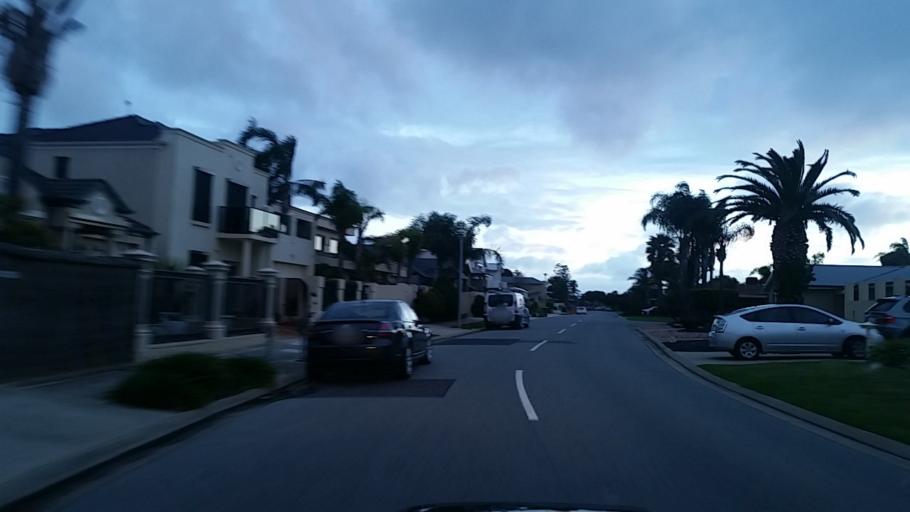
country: AU
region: South Australia
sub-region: Charles Sturt
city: West Lakes Shore
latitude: -34.8667
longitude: 138.4884
